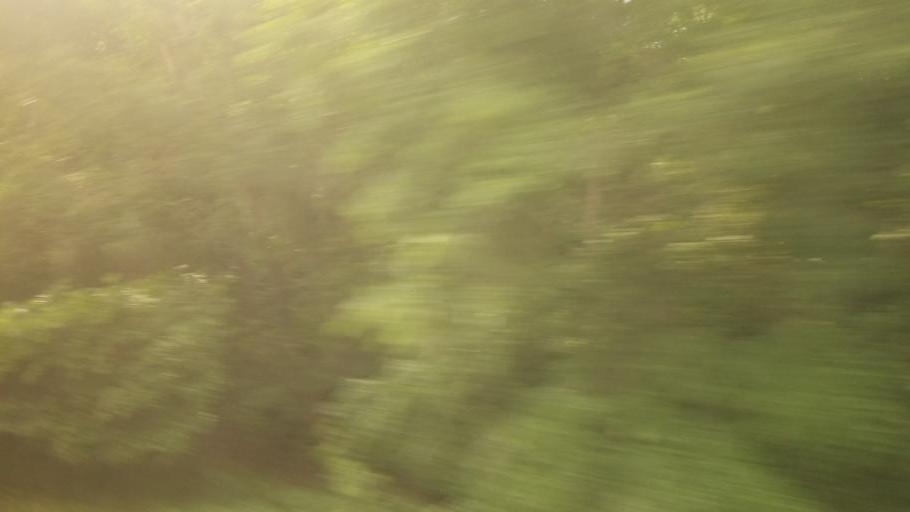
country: US
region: Kansas
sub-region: Johnson County
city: De Soto
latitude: 38.9784
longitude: -95.0141
